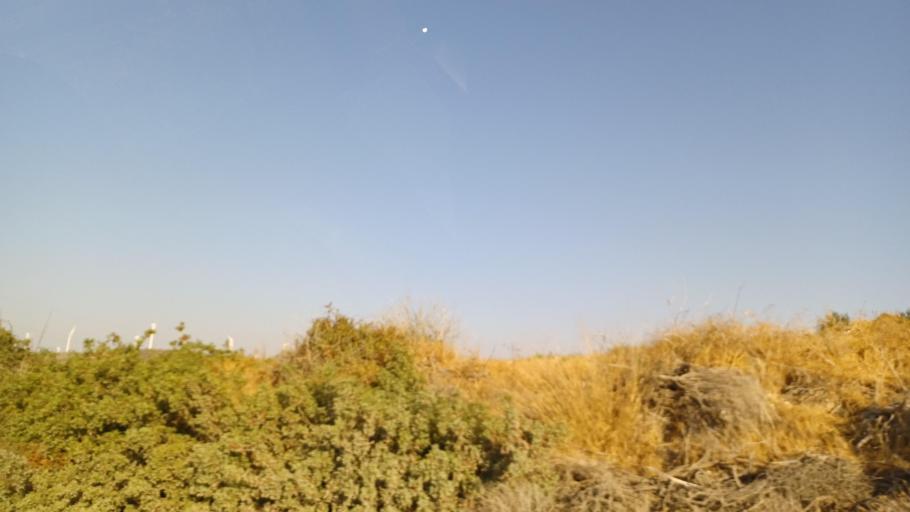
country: CY
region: Limassol
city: Pissouri
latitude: 34.7200
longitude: 32.6755
